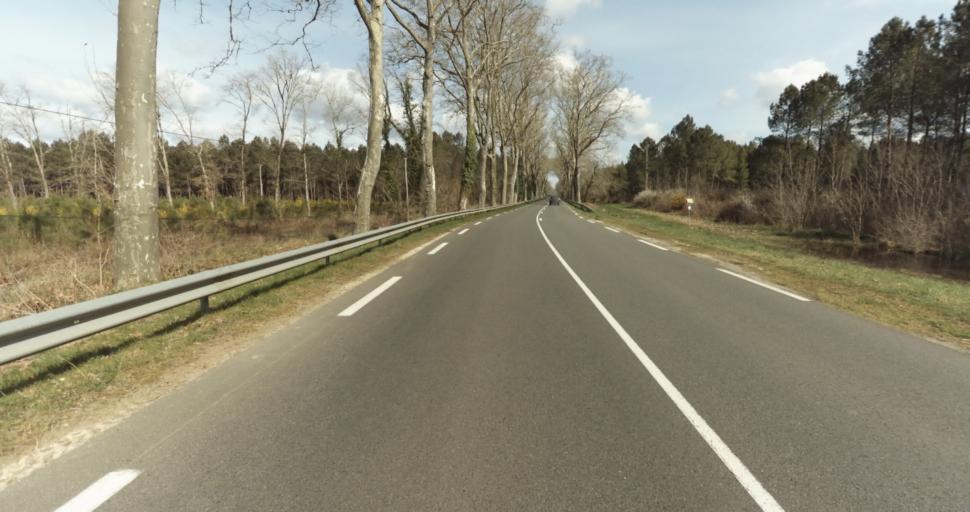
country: FR
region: Aquitaine
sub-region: Departement des Landes
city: Roquefort
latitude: 44.0610
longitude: -0.3172
